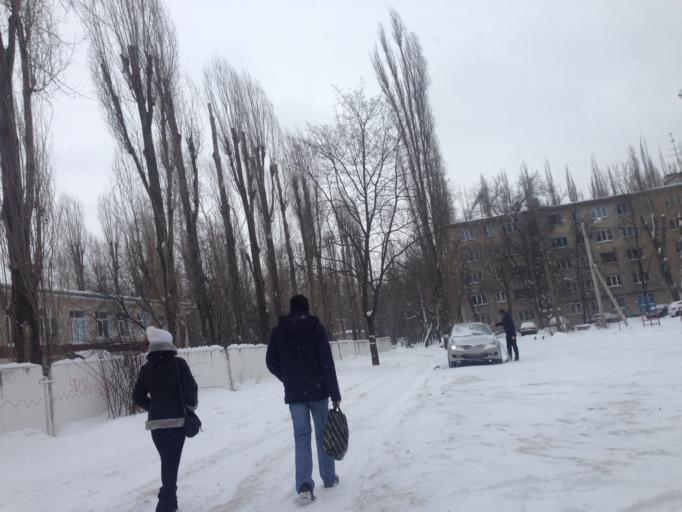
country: RU
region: Voronezj
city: Voronezh
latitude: 51.6571
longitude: 39.1531
